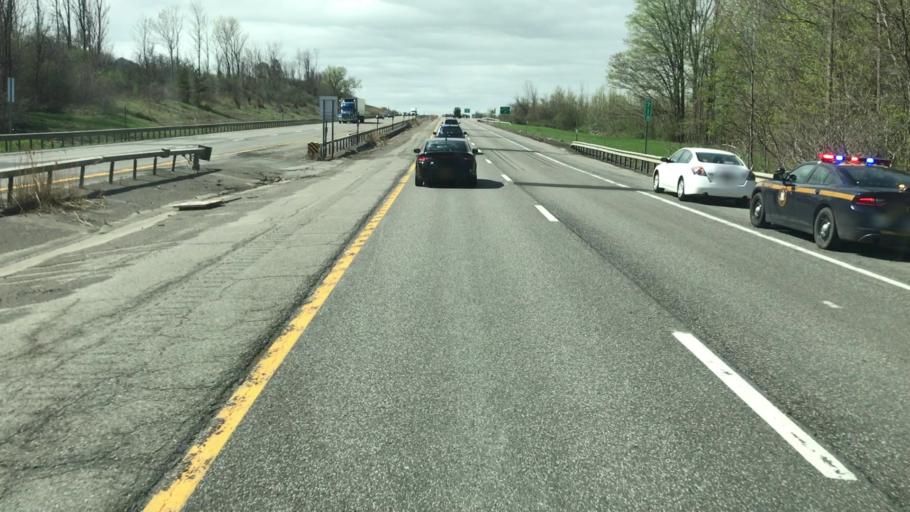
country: US
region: New York
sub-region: Onondaga County
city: Nedrow
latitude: 42.8650
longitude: -76.1150
